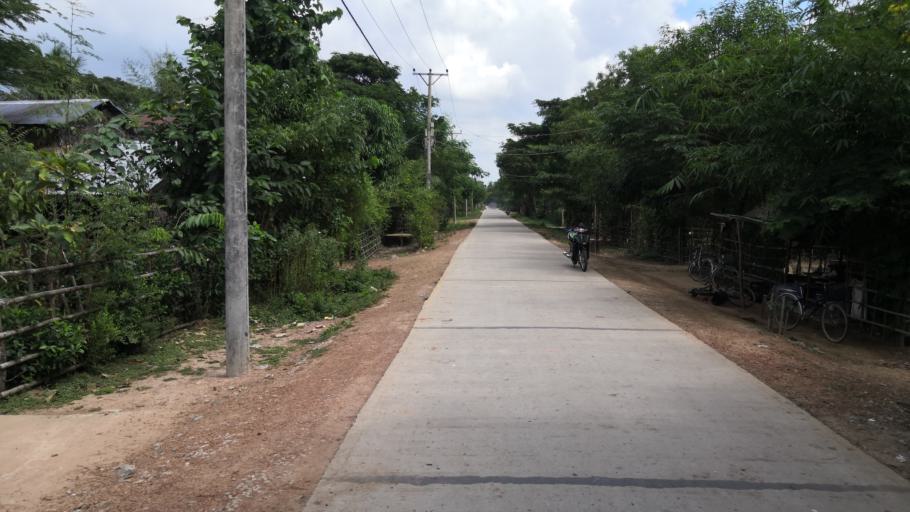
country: MM
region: Yangon
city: Kanbe
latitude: 16.4349
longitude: 96.1607
